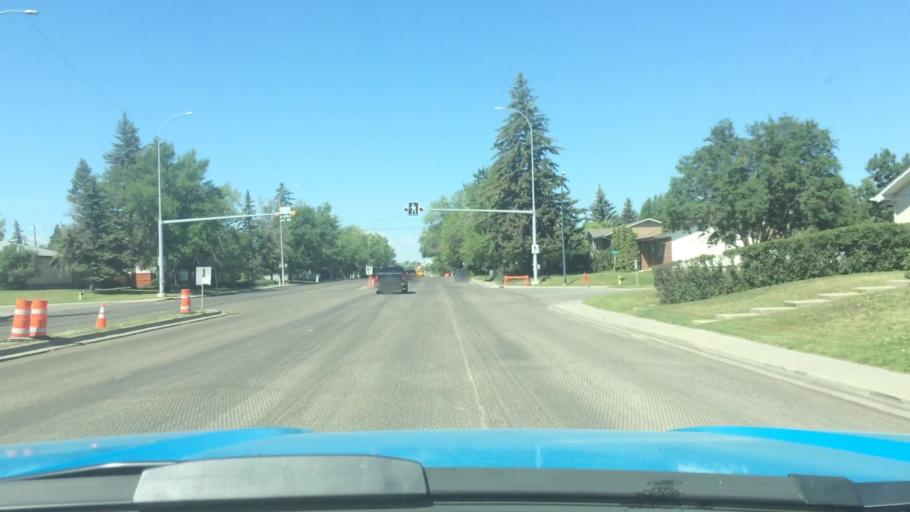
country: CA
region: Alberta
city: Calgary
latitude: 51.0529
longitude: -113.9628
